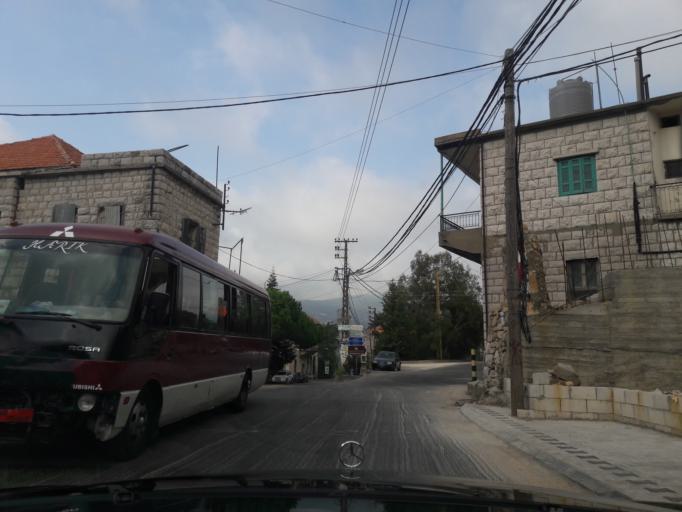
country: LB
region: Mont-Liban
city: Djounie
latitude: 33.9263
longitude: 35.7371
